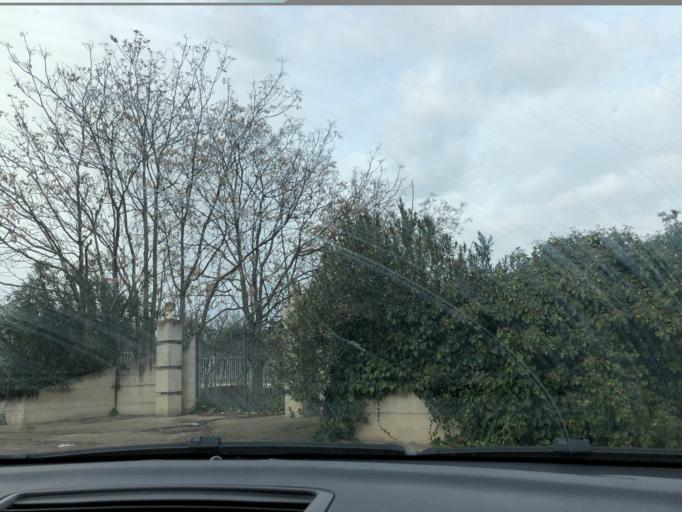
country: IT
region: Apulia
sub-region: Provincia di Foggia
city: Lucera
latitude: 41.5019
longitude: 15.3538
